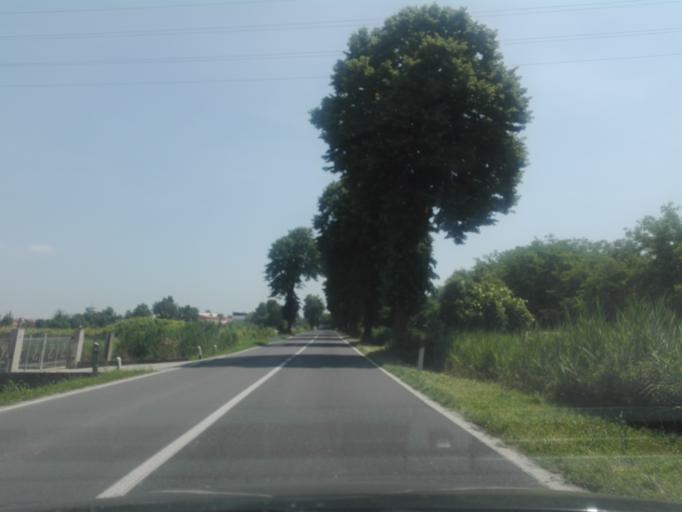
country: IT
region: Veneto
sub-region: Provincia di Rovigo
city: Adria
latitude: 45.0611
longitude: 12.0408
